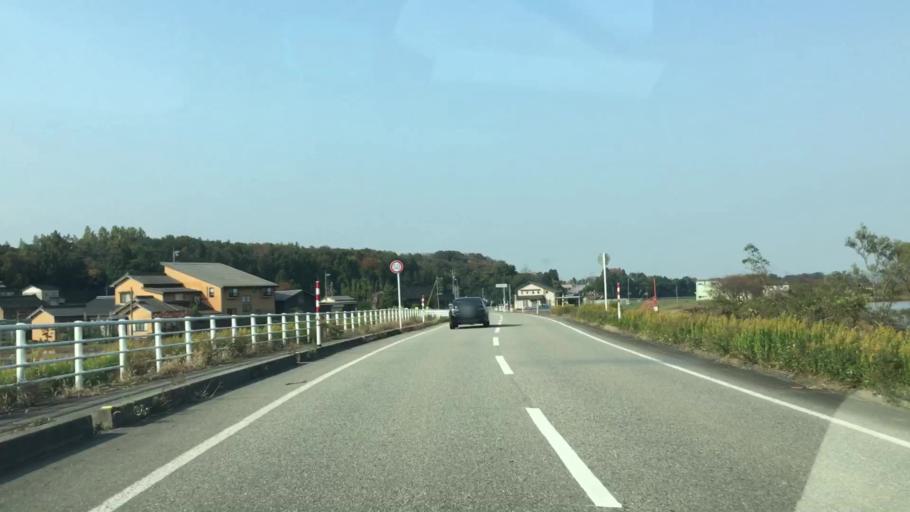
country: JP
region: Toyama
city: Toyama-shi
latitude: 36.6011
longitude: 137.2495
